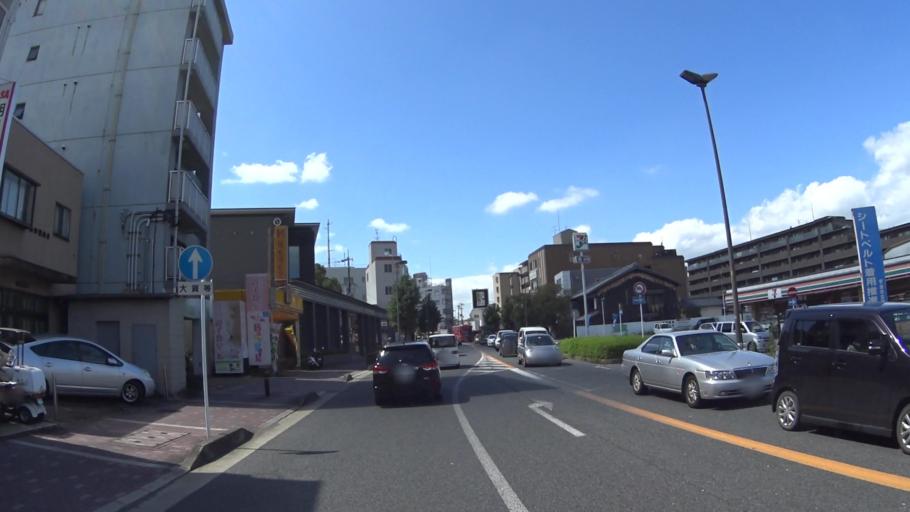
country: JP
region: Kyoto
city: Uji
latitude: 34.8898
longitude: 135.8009
